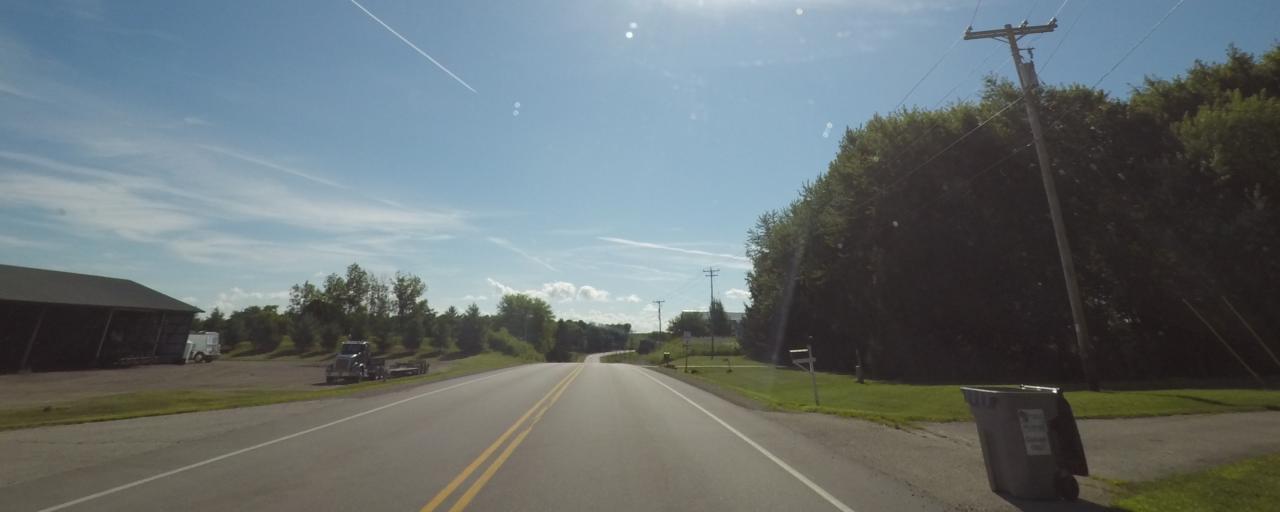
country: US
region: Wisconsin
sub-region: Jefferson County
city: Johnson Creek
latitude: 43.0755
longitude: -88.7211
